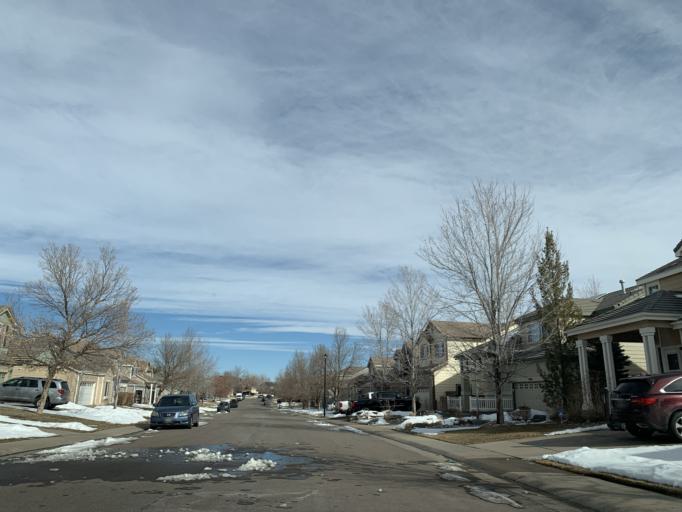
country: US
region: Colorado
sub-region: Douglas County
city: Carriage Club
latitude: 39.5254
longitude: -104.9317
